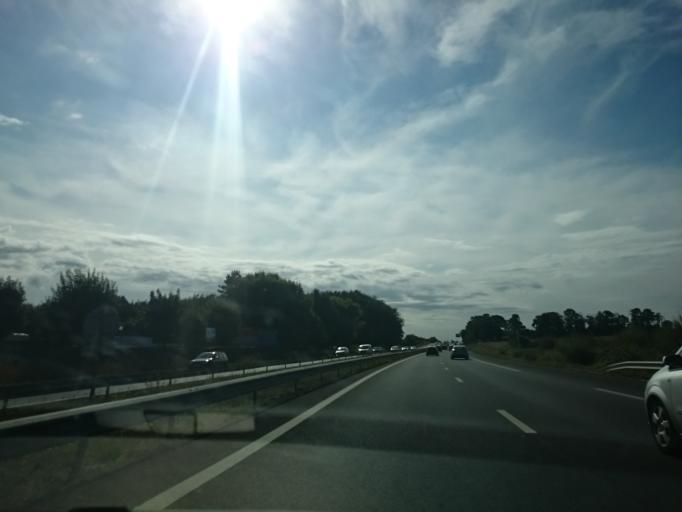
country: FR
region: Brittany
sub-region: Departement d'Ille-et-Vilaine
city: Pace
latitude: 48.1433
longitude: -1.7790
